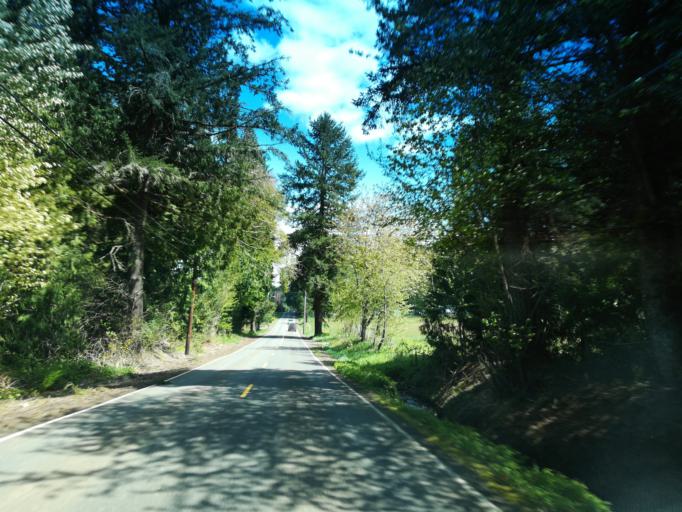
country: US
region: Oregon
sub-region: Clackamas County
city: Damascus
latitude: 45.4397
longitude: -122.4221
